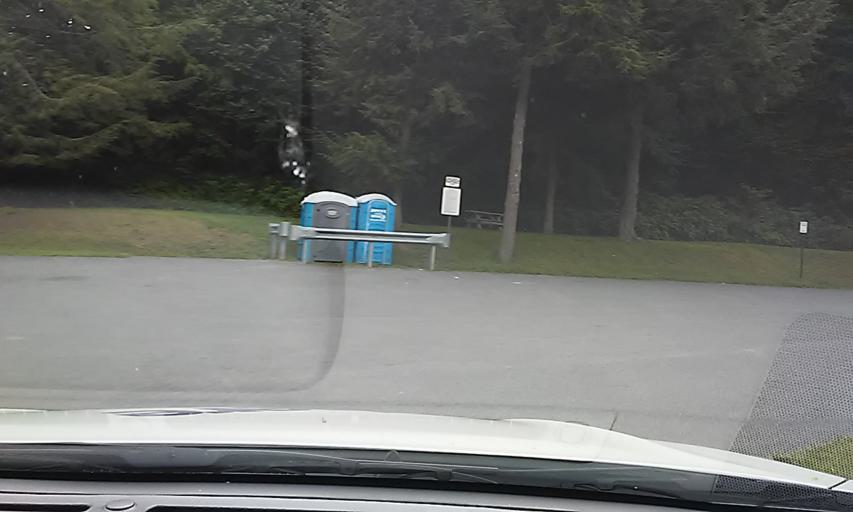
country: US
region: Pennsylvania
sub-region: Potter County
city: Galeton
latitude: 41.7784
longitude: -77.8285
